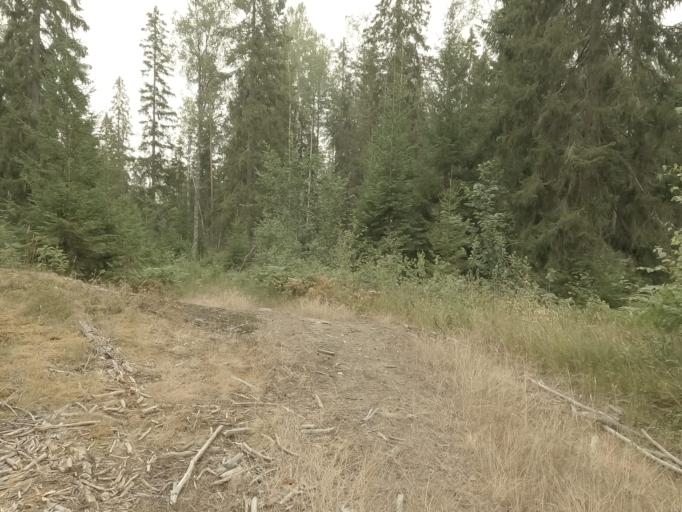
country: RU
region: Leningrad
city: Kamennogorsk
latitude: 61.0496
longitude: 29.1828
